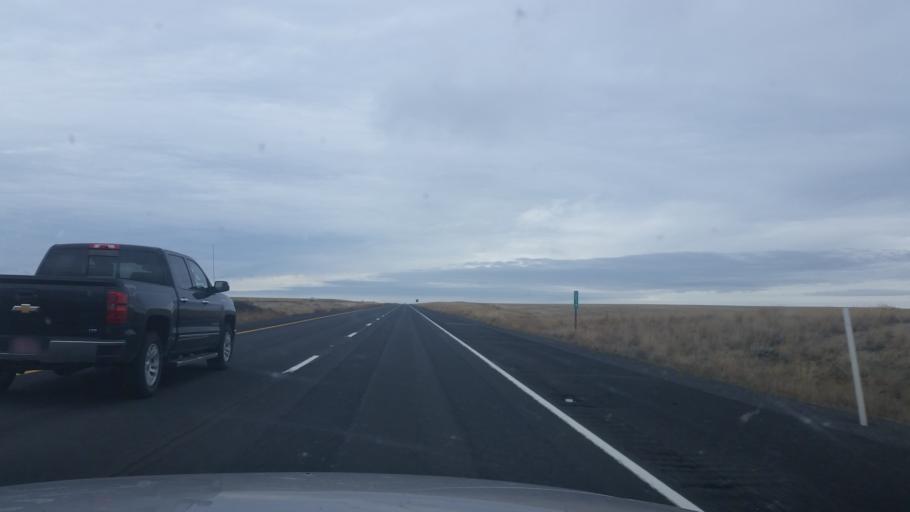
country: US
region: Washington
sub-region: Adams County
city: Ritzville
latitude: 47.1116
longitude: -118.4562
